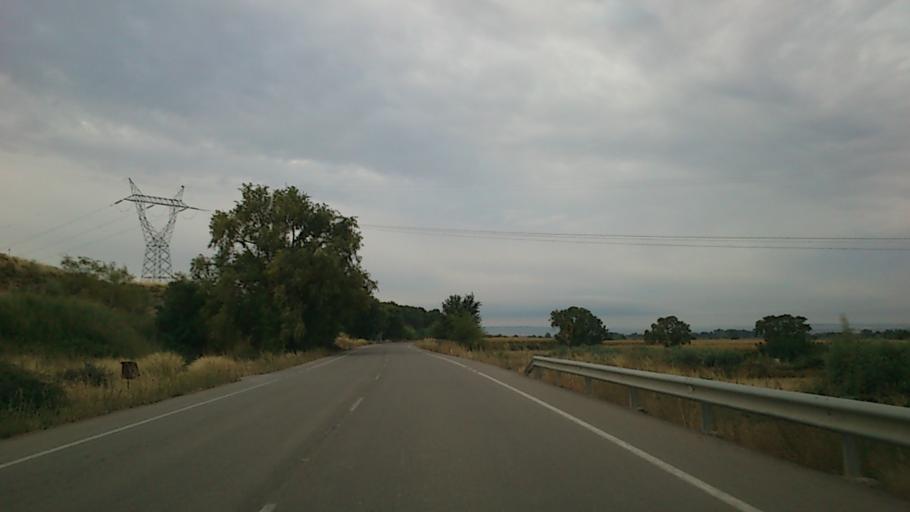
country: ES
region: Aragon
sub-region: Provincia de Zaragoza
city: San Mateo de Gallego
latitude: 41.7926
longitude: -0.7826
